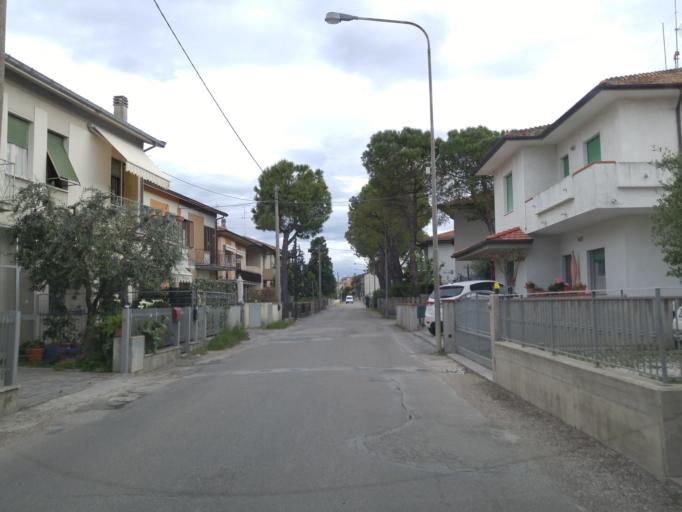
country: IT
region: The Marches
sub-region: Provincia di Pesaro e Urbino
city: Rosciano
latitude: 43.8263
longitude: 13.0059
